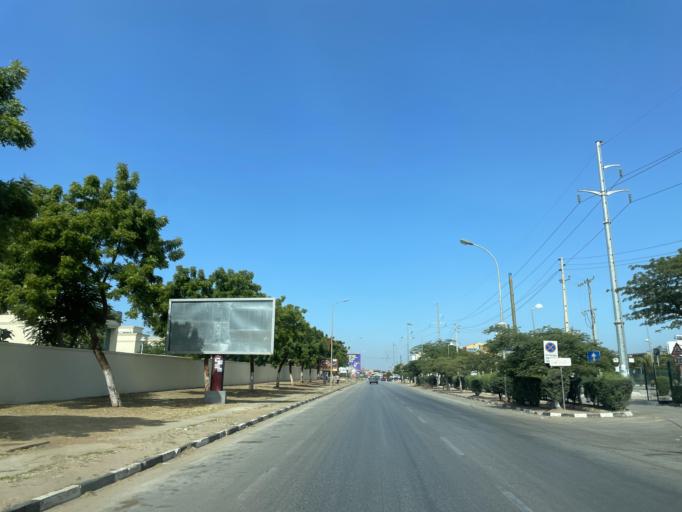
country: AO
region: Luanda
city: Luanda
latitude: -8.9161
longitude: 13.1977
